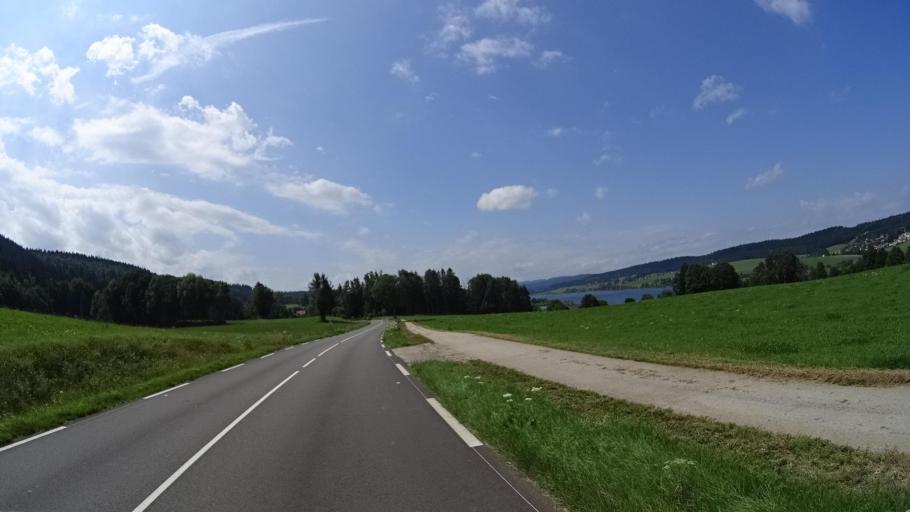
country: FR
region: Franche-Comte
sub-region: Departement du Doubs
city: Les Fourgs
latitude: 46.8228
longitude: 6.3317
